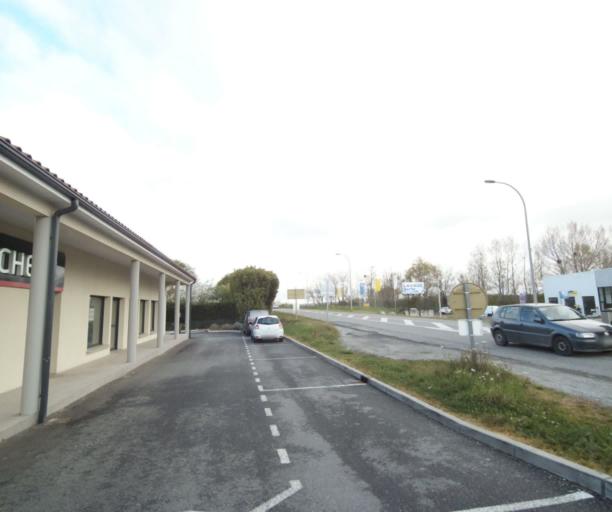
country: FR
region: Midi-Pyrenees
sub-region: Departement de l'Ariege
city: Saverdun
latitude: 43.2466
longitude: 1.5686
